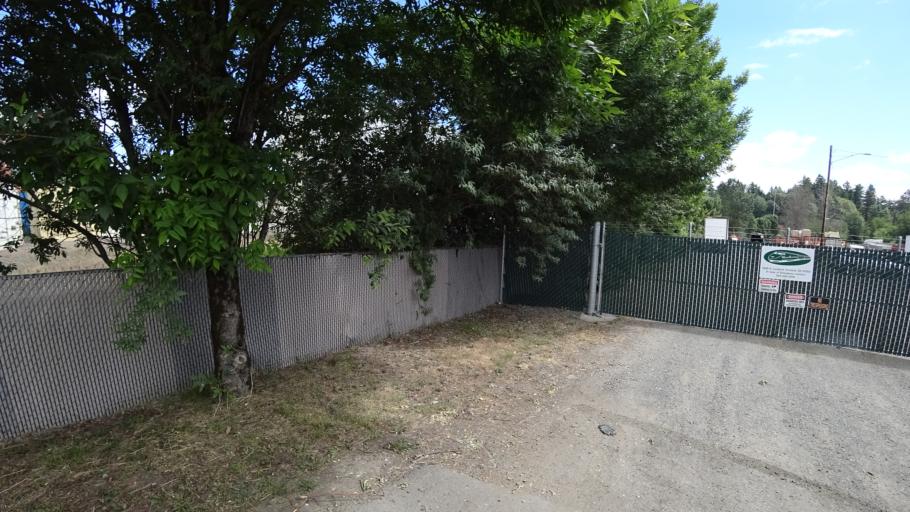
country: US
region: Oregon
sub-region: Washington County
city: West Haven
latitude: 45.6070
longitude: -122.7663
